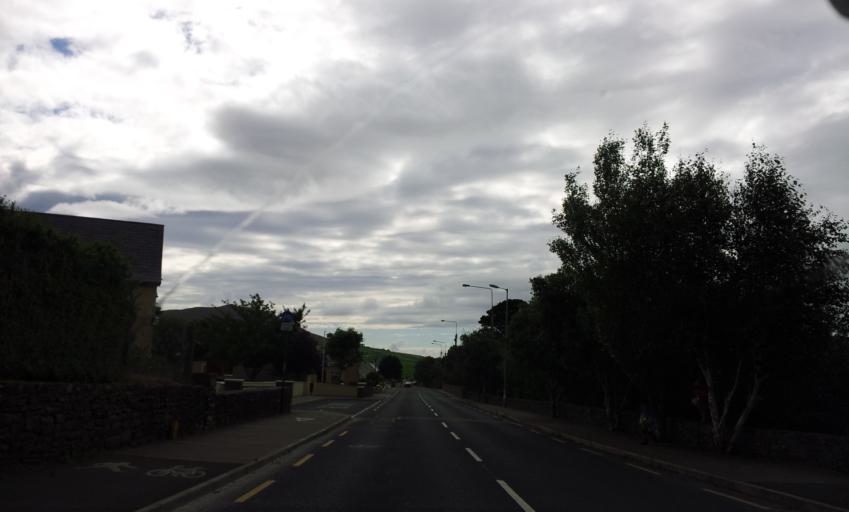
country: IE
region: Munster
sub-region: Ciarrai
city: Dingle
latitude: 52.1541
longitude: -10.0473
